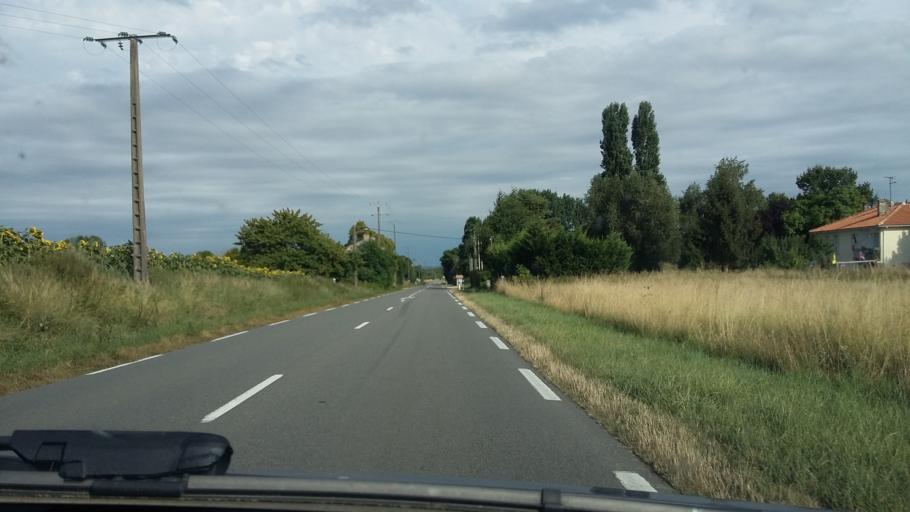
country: FR
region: Poitou-Charentes
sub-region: Departement de la Charente
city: Asnieres-sur-Nouere
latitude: 45.7081
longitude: 0.0819
